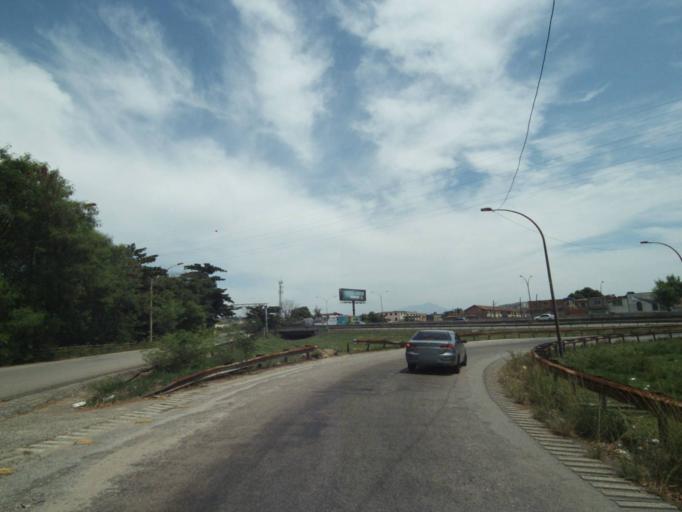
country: BR
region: Rio de Janeiro
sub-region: Duque De Caxias
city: Duque de Caxias
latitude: -22.7992
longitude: -43.3098
